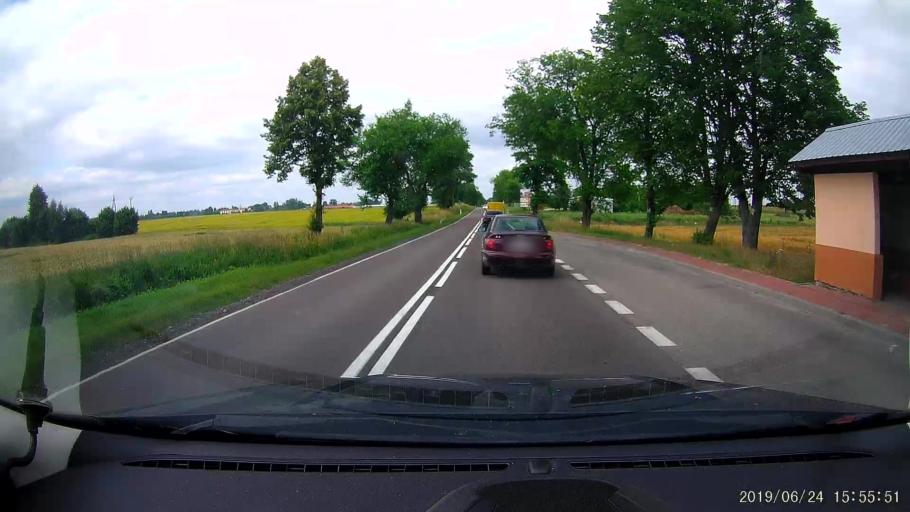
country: PL
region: Subcarpathian Voivodeship
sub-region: Powiat lubaczowski
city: Cieszanow
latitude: 50.2336
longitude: 23.1257
